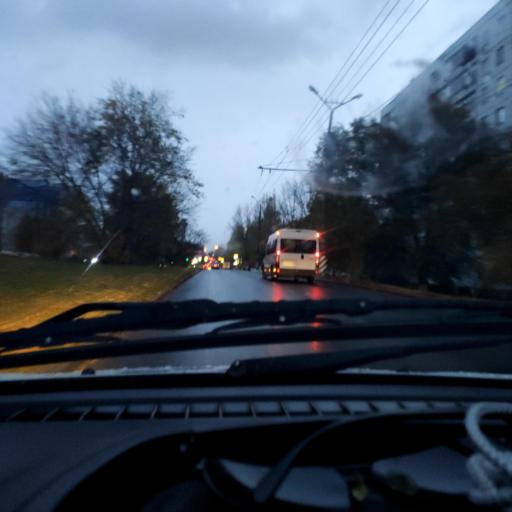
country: RU
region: Samara
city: Zhigulevsk
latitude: 53.4798
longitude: 49.4741
